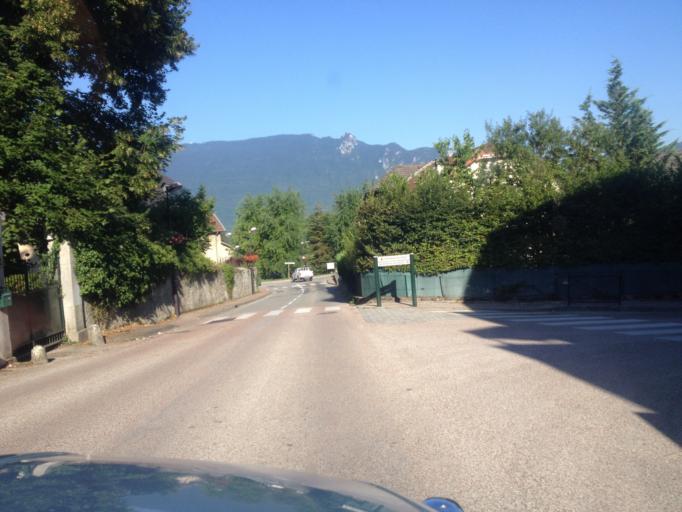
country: FR
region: Rhone-Alpes
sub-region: Departement de la Savoie
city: Drumettaz-Clarafond
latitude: 45.6598
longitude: 5.9221
